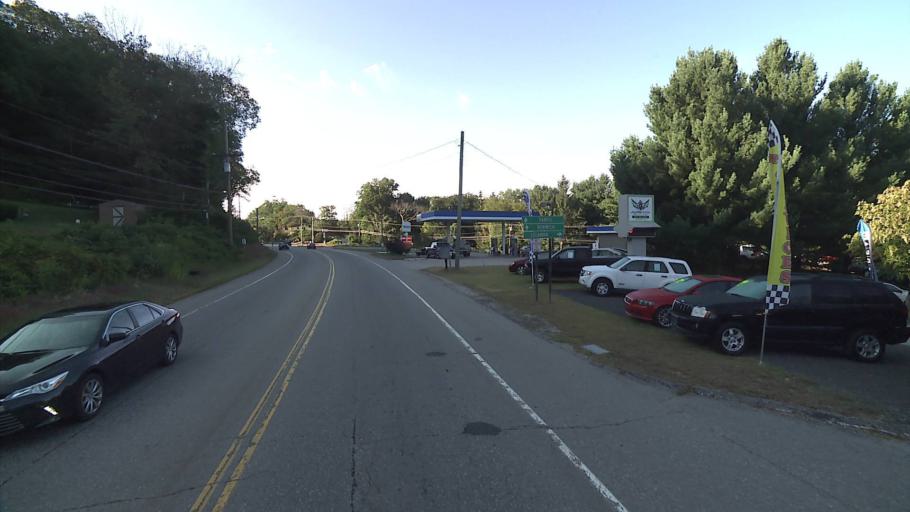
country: US
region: Connecticut
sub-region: New London County
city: Baltic
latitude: 41.5711
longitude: -72.1322
